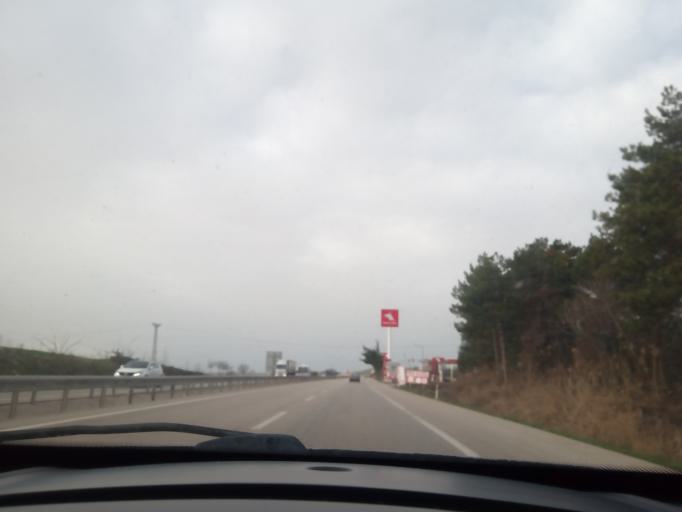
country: TR
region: Bursa
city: Gorukle
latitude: 40.2145
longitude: 28.7414
